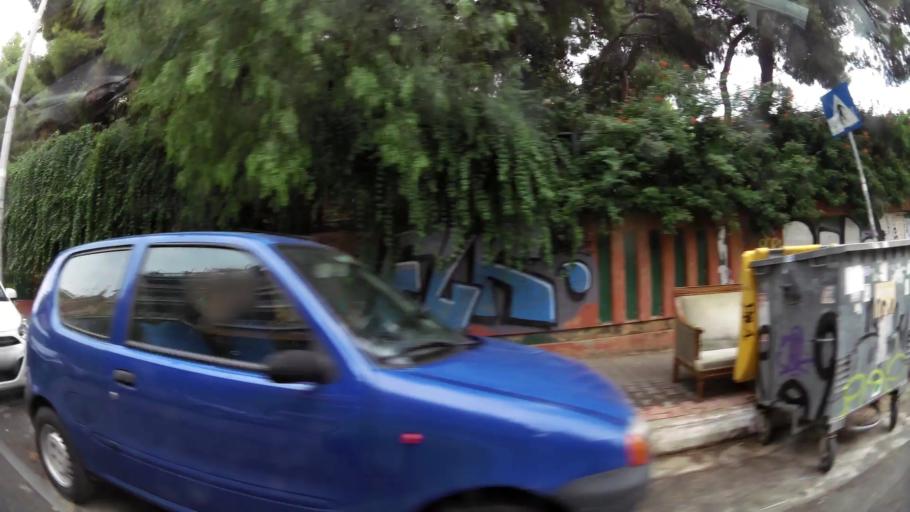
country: GR
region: Attica
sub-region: Nomarchia Athinas
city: Vyronas
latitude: 37.9614
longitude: 23.7550
